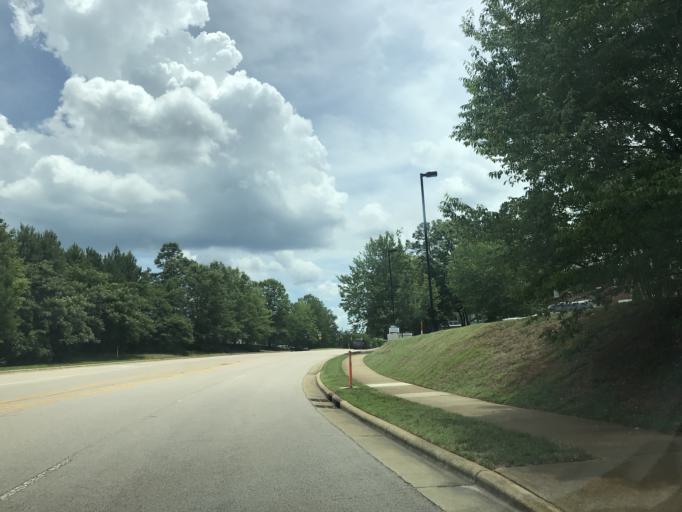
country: US
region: North Carolina
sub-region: Wake County
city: West Raleigh
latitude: 35.9067
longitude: -78.6582
